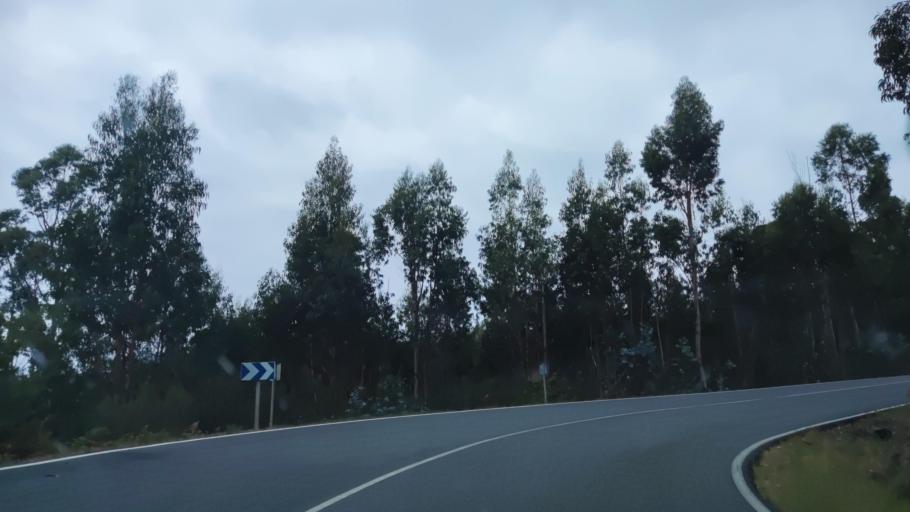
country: ES
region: Galicia
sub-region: Provincia de Pontevedra
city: Catoira
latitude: 42.6520
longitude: -8.7584
